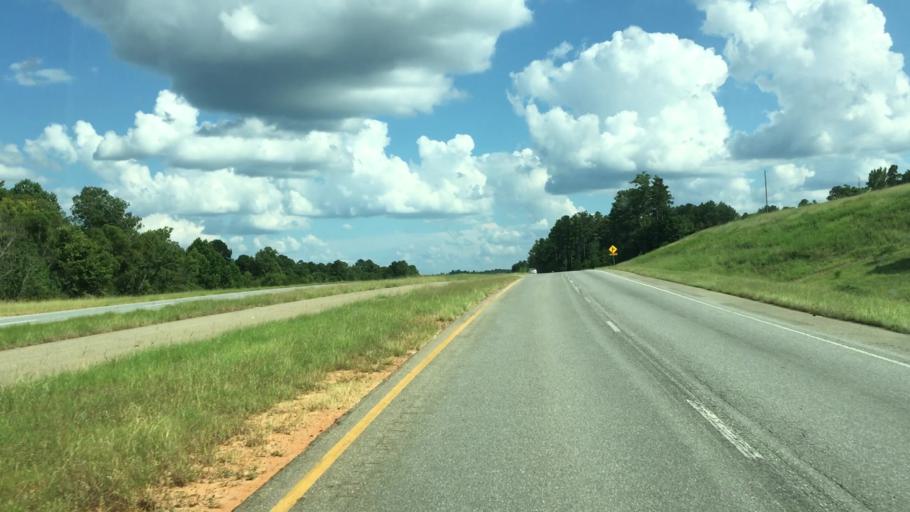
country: US
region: Georgia
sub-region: Wilkinson County
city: Irwinton
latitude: 32.7087
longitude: -83.1335
